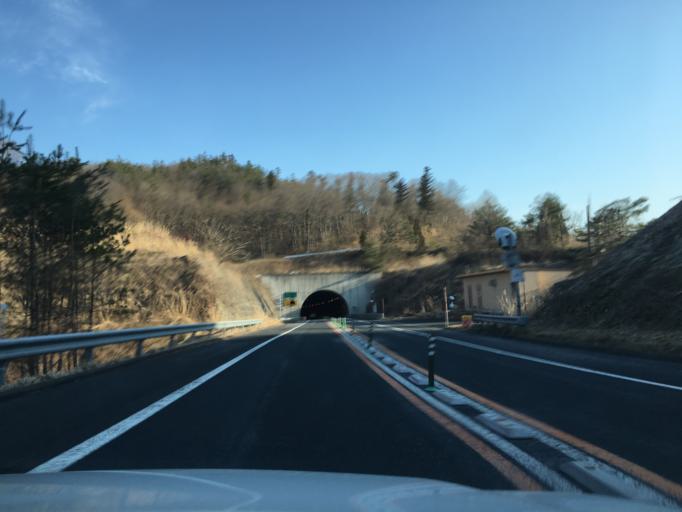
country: JP
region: Yamagata
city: Sagae
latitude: 38.3874
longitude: 140.2208
